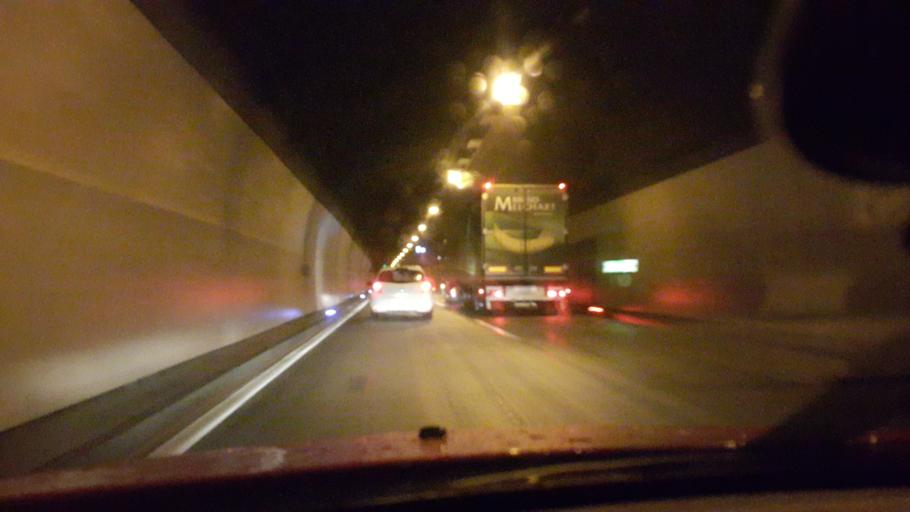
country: SI
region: Slovenska Konjice
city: Slovenske Konjice
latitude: 46.3151
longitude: 15.4582
